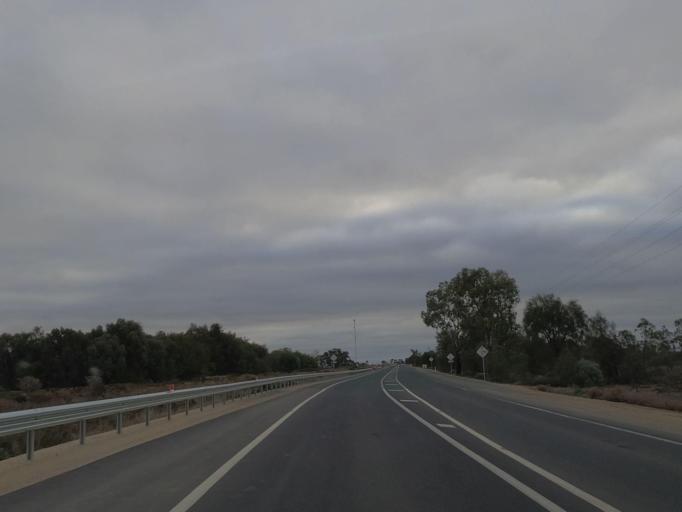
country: AU
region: Victoria
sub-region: Swan Hill
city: Swan Hill
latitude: -35.5357
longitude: 143.7452
